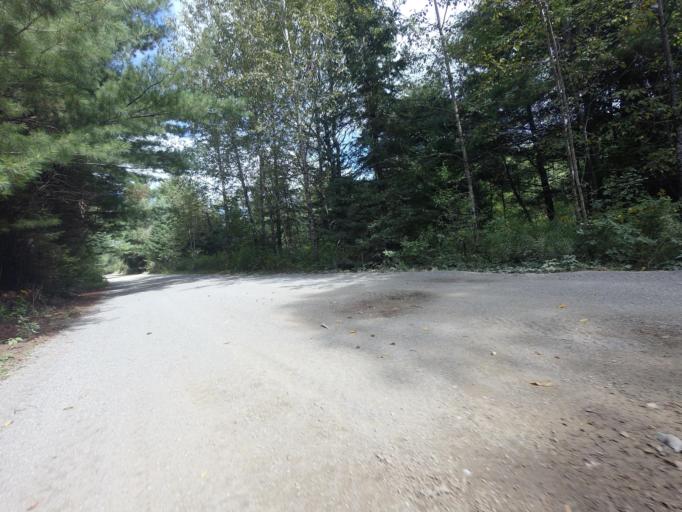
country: CA
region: Ontario
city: Omemee
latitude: 44.7479
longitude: -78.6665
